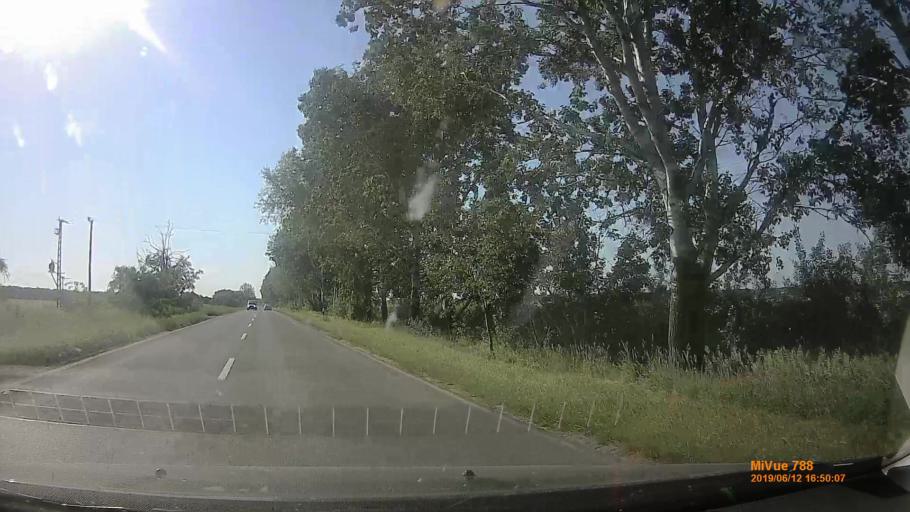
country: HU
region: Csongrad
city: Kiszombor
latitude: 46.1973
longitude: 20.3998
